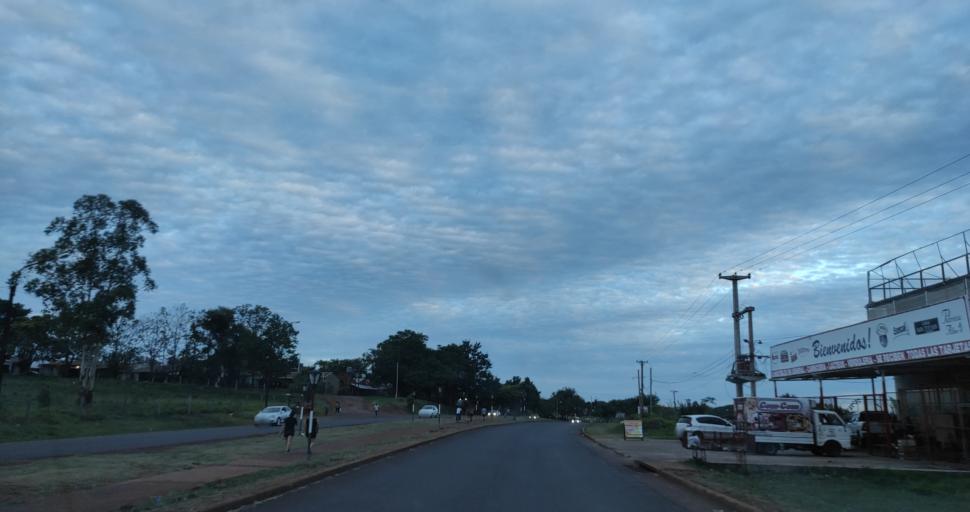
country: AR
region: Misiones
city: Garupa
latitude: -27.4693
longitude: -55.8478
